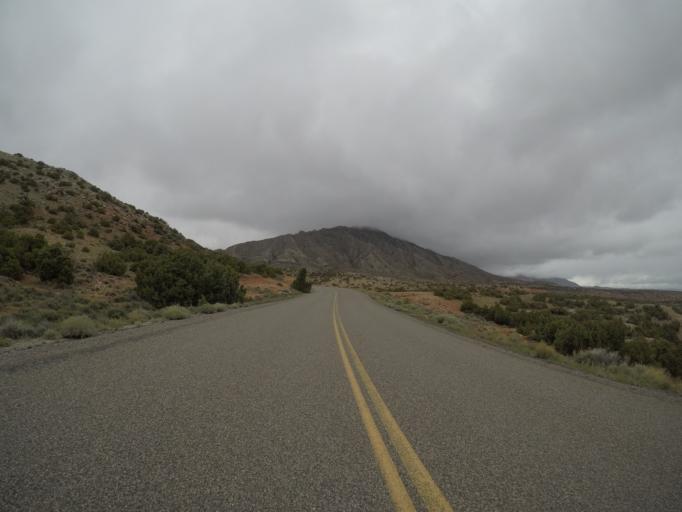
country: US
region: Wyoming
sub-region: Big Horn County
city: Lovell
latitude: 45.0250
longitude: -108.2588
